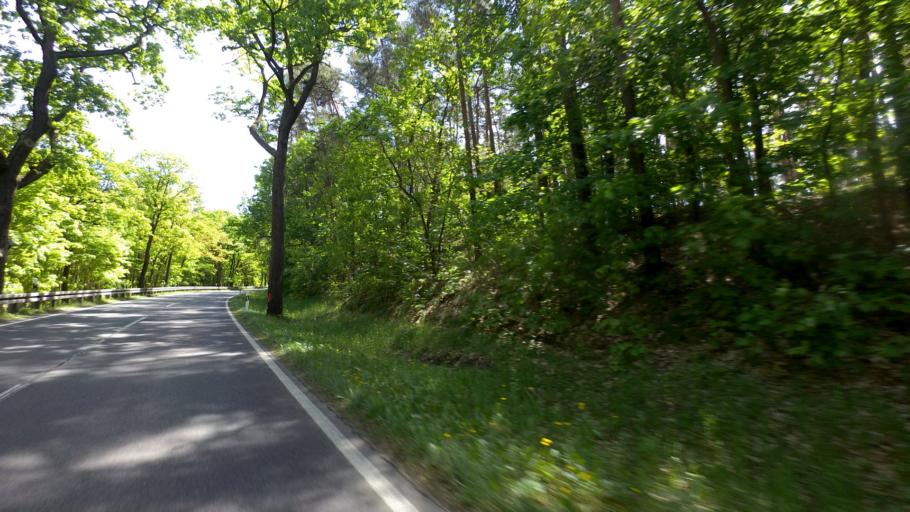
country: DE
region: Brandenburg
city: Luckenwalde
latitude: 52.0710
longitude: 13.1969
